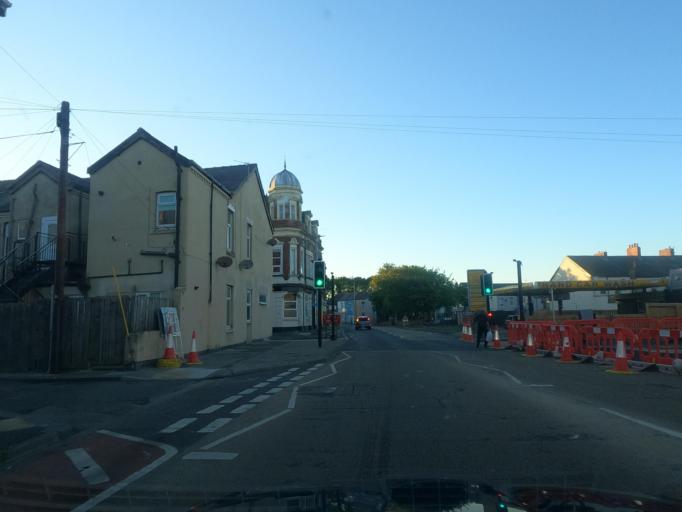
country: GB
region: England
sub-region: Northumberland
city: Blyth
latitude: 55.1259
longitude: -1.5169
